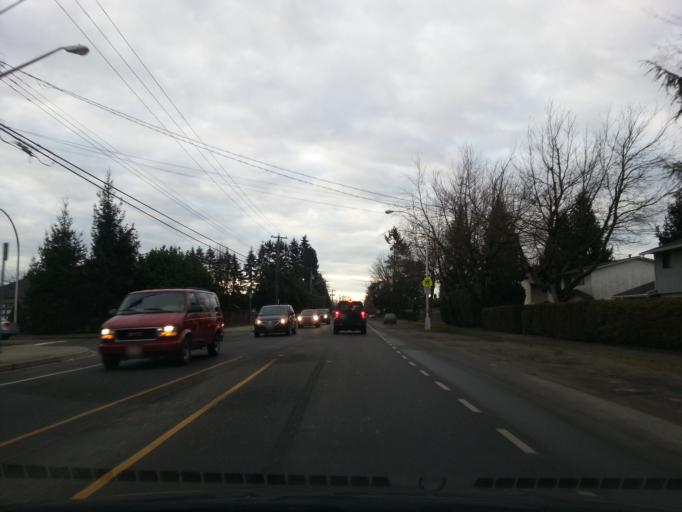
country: CA
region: British Columbia
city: Langley
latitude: 49.1177
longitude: -122.7126
